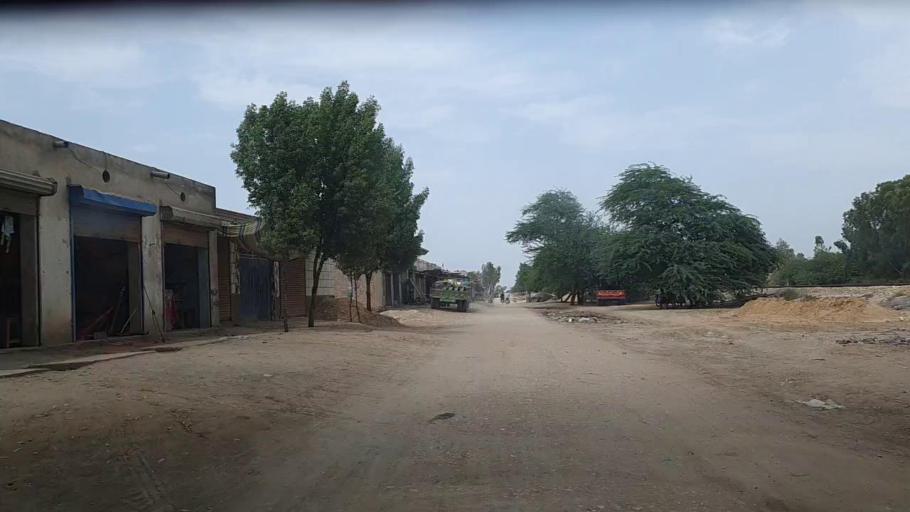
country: PK
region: Sindh
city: Bhiria
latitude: 26.8963
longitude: 68.2868
